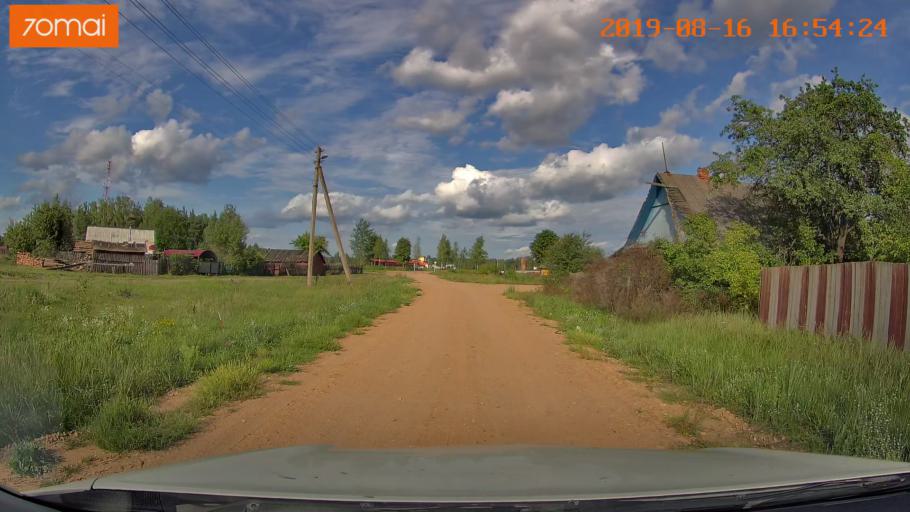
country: BY
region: Mogilev
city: Asipovichy
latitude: 53.2551
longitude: 28.8077
